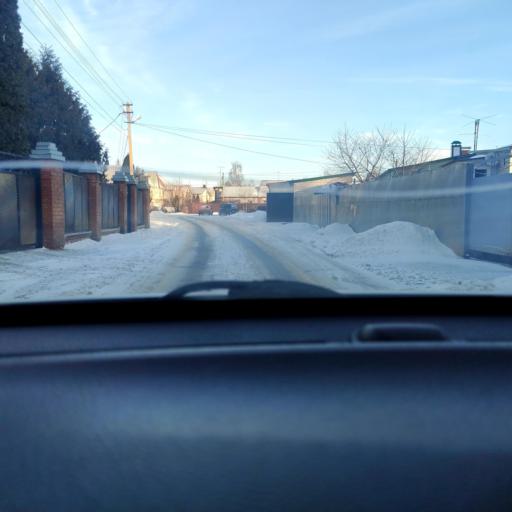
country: RU
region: Voronezj
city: Voronezh
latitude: 51.7407
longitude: 39.2613
